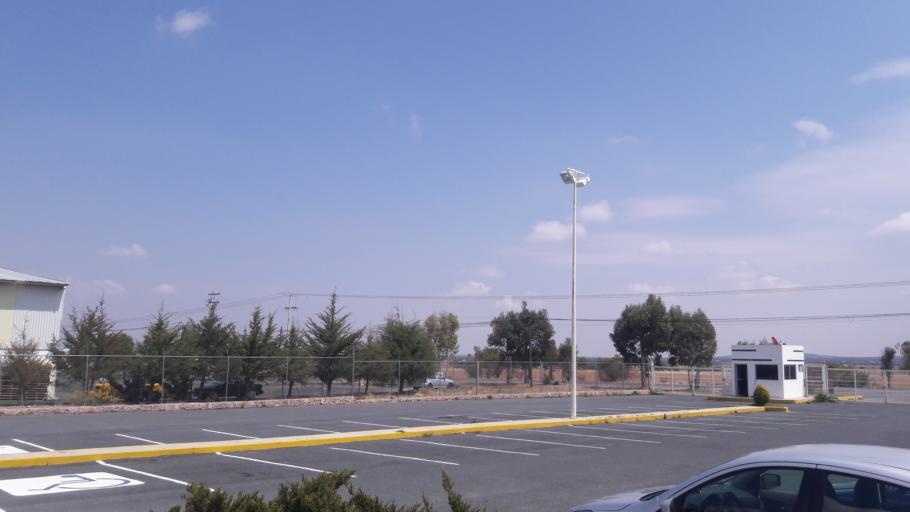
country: MX
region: Zacatecas
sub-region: Guadalupe
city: Martinez Dominguez
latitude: 22.6991
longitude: -102.4890
